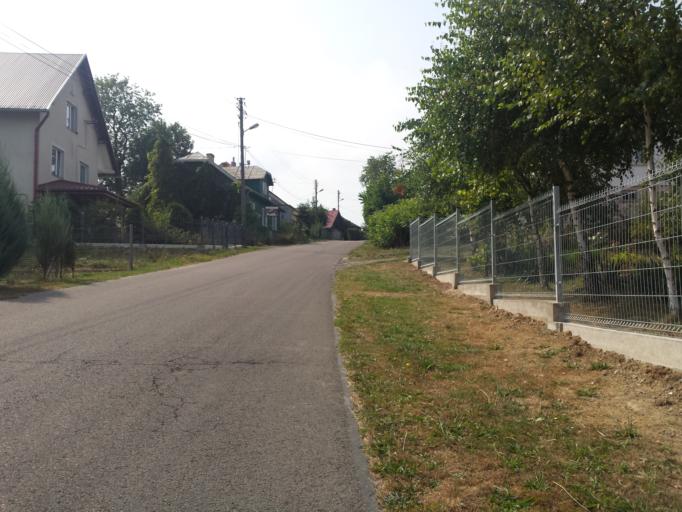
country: PL
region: Subcarpathian Voivodeship
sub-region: Powiat rzeszowski
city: Dynow
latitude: 49.8186
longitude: 22.2114
